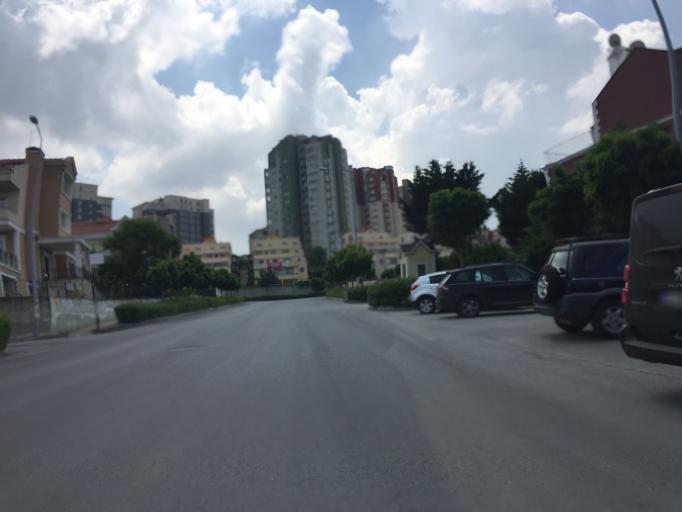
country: TR
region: Istanbul
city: Esenyurt
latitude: 41.0798
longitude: 28.6674
